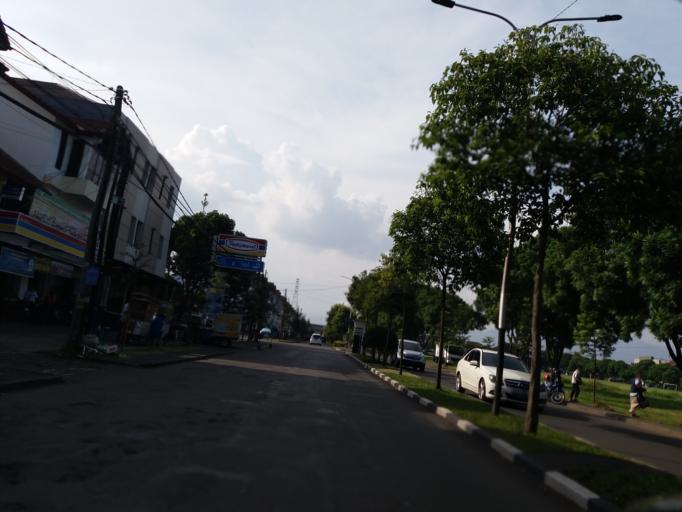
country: ID
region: West Java
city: Bandung
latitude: -6.9570
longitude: 107.6268
